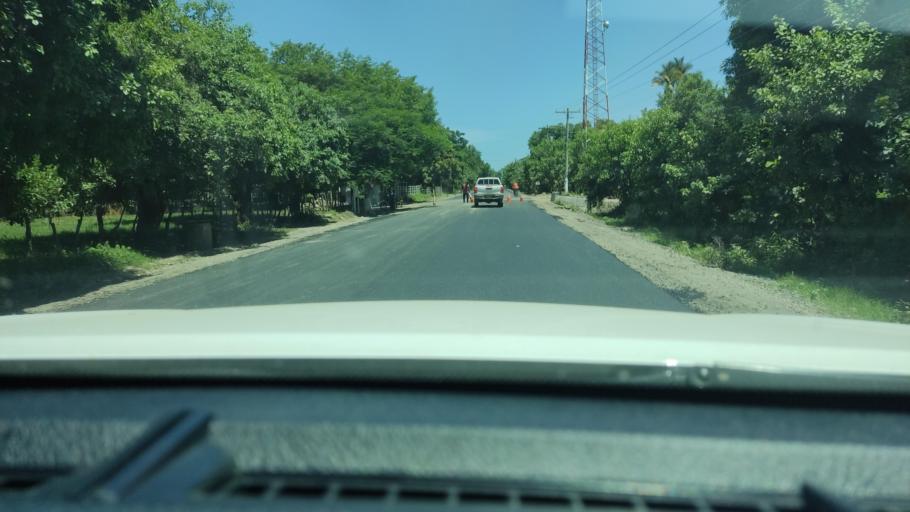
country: SV
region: Ahuachapan
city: San Francisco Menendez
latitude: 13.8289
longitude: -90.1188
